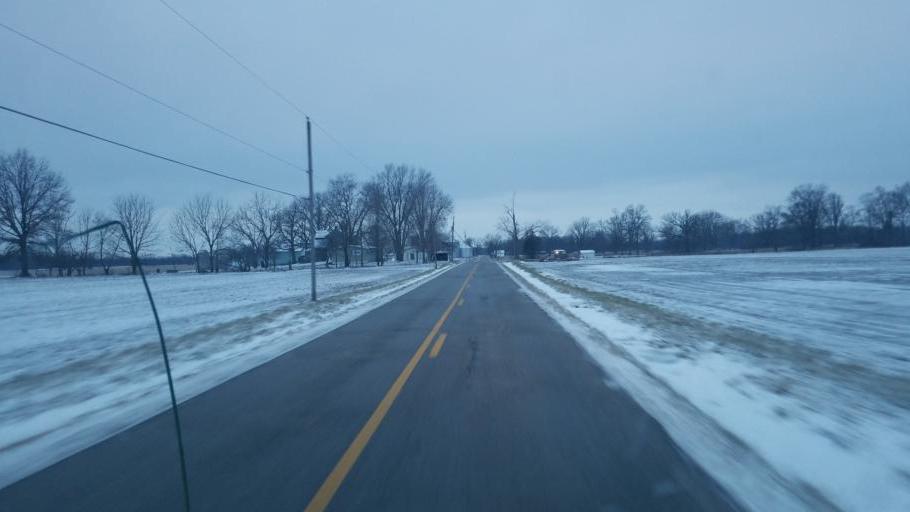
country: US
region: Ohio
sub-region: Delaware County
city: Sunbury
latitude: 40.2044
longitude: -82.8308
